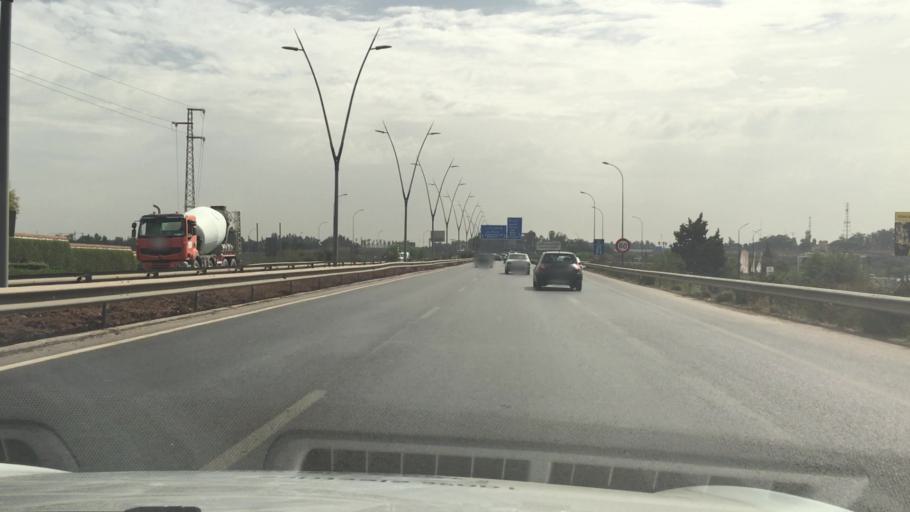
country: MA
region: Grand Casablanca
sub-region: Nouaceur
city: Bouskoura
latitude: 33.5037
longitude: -7.6291
